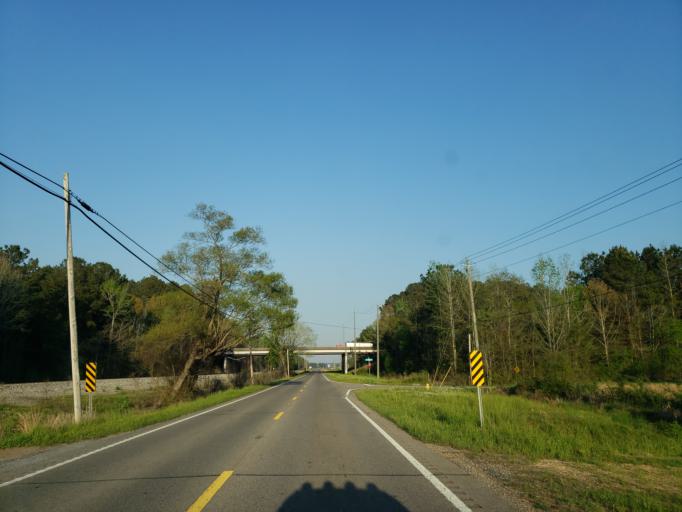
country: US
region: Mississippi
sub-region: Lauderdale County
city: Marion
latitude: 32.3941
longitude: -88.6415
